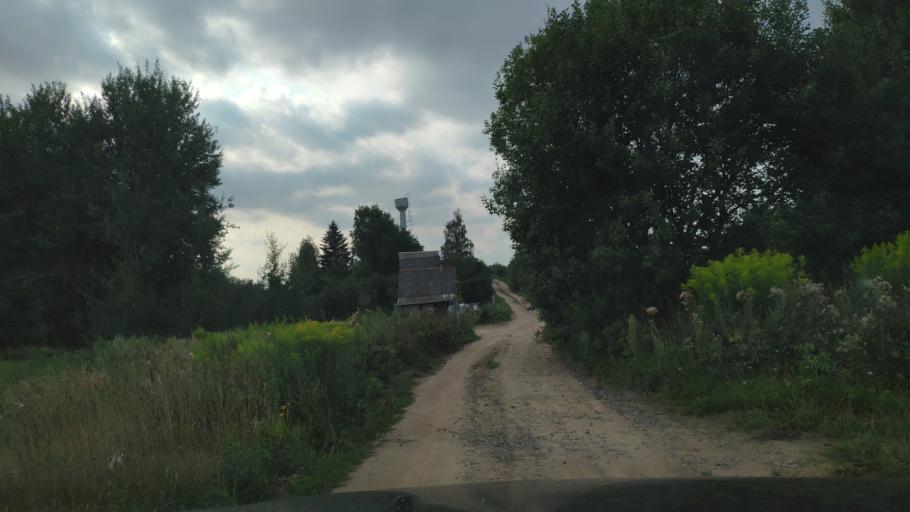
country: BY
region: Minsk
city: Khatsyezhyna
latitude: 53.8546
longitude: 27.2937
